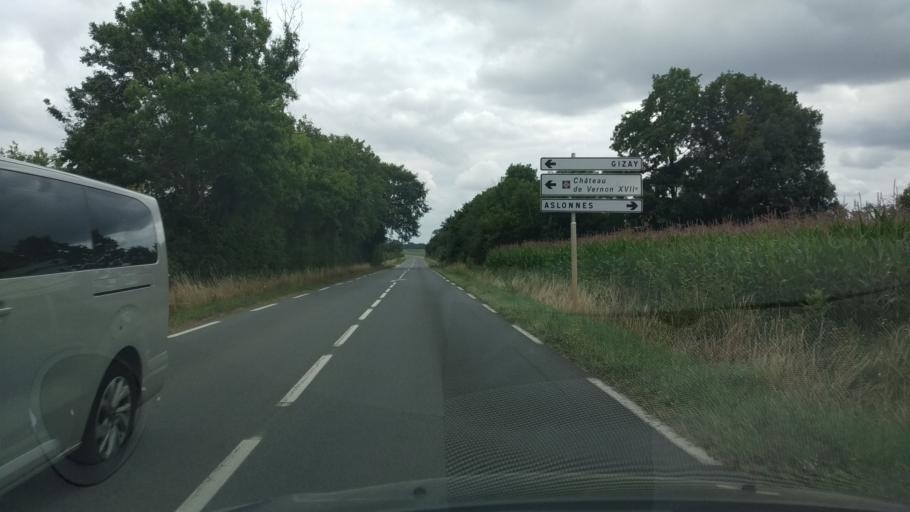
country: FR
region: Poitou-Charentes
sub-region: Departement de la Vienne
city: La Villedieu-du-Clain
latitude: 46.4438
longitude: 0.3702
